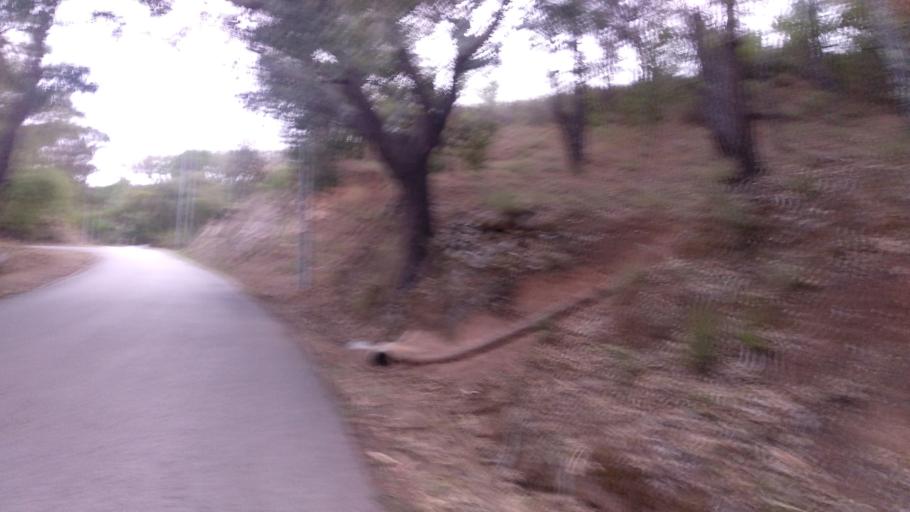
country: PT
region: Faro
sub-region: Sao Bras de Alportel
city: Sao Bras de Alportel
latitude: 37.1816
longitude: -7.9132
